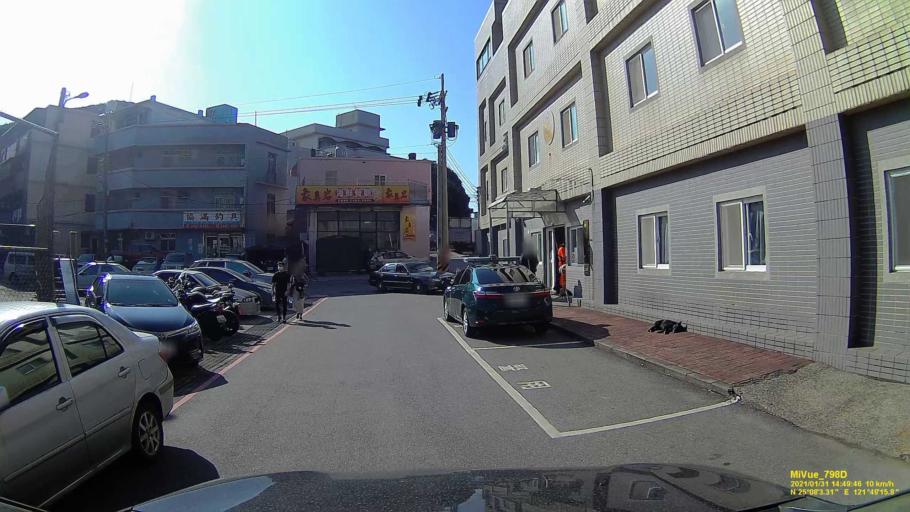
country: TW
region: Taiwan
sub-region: Keelung
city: Keelung
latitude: 25.1343
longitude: 121.8209
